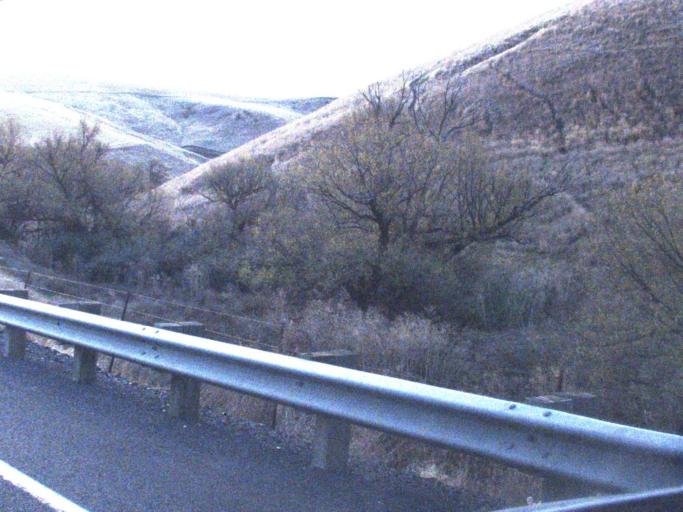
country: US
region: Washington
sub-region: Garfield County
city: Pomeroy
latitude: 46.6681
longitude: -117.8004
